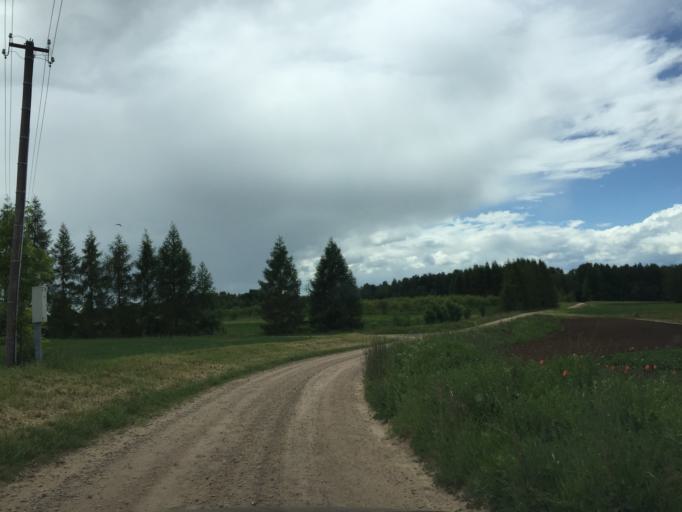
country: LV
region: Lecava
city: Iecava
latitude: 56.5579
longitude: 24.1604
